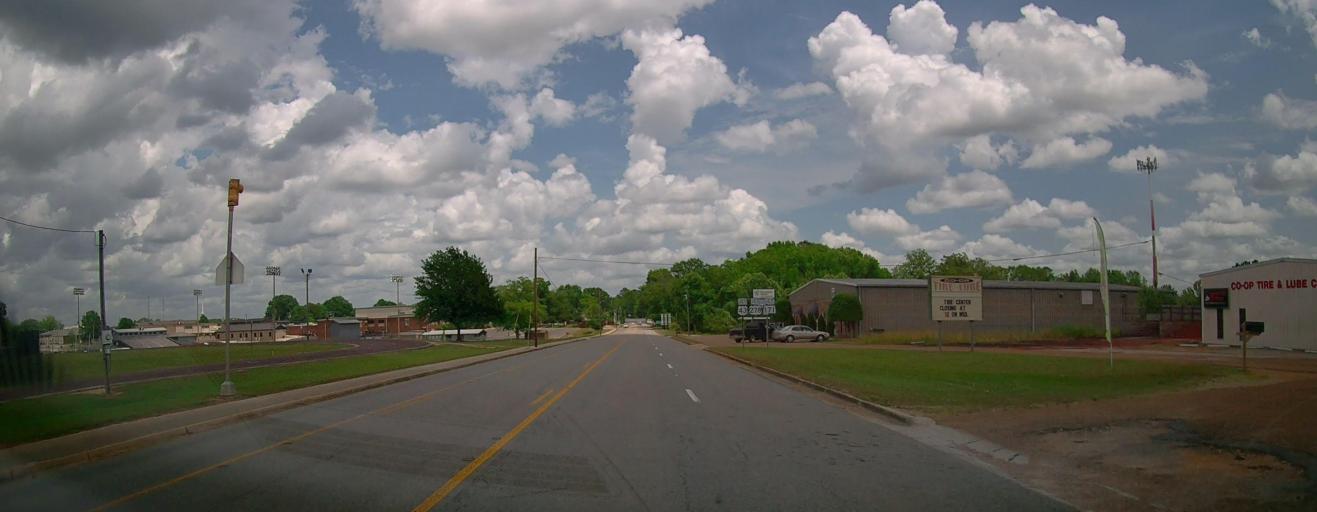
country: US
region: Alabama
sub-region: Marion County
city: Hamilton
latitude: 34.1376
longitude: -87.9948
